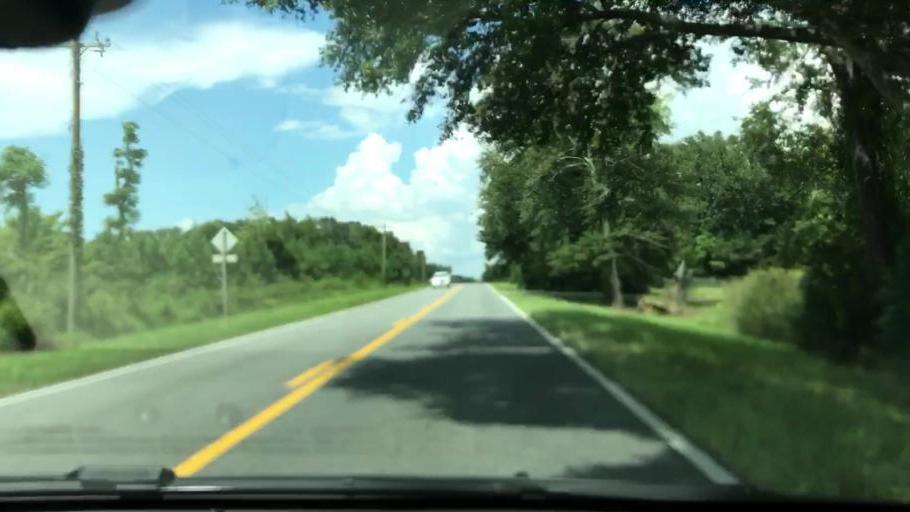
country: US
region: Florida
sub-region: Jackson County
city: Malone
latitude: 30.9501
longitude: -85.1182
